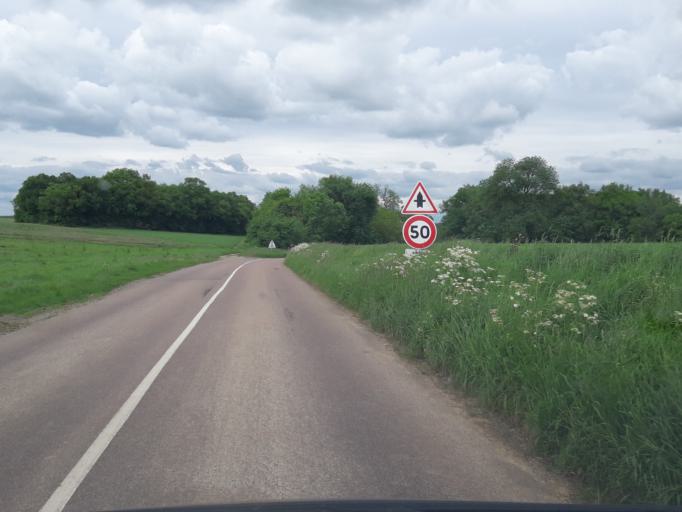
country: FR
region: Ile-de-France
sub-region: Departement de l'Essonne
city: Saclas
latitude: 48.3494
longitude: 2.1399
